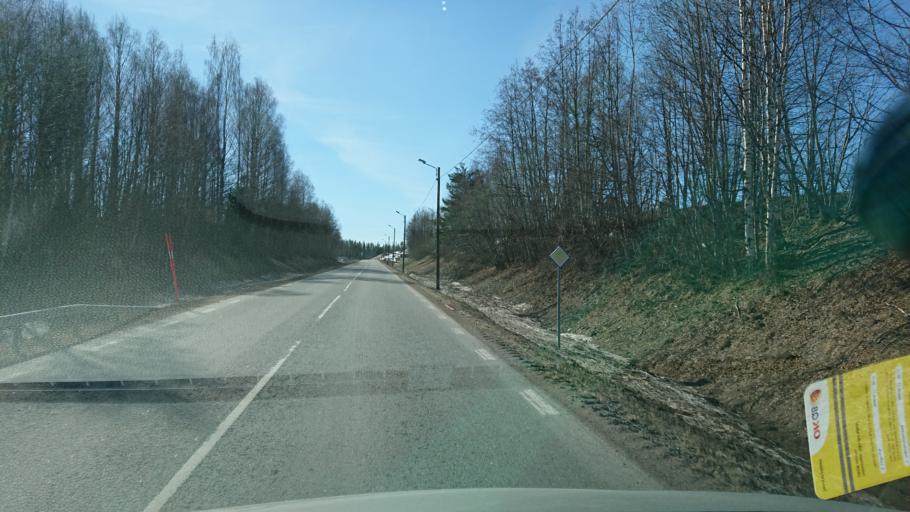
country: SE
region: Vaesternorrland
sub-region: Solleftea Kommun
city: As
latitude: 63.6477
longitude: 16.4585
